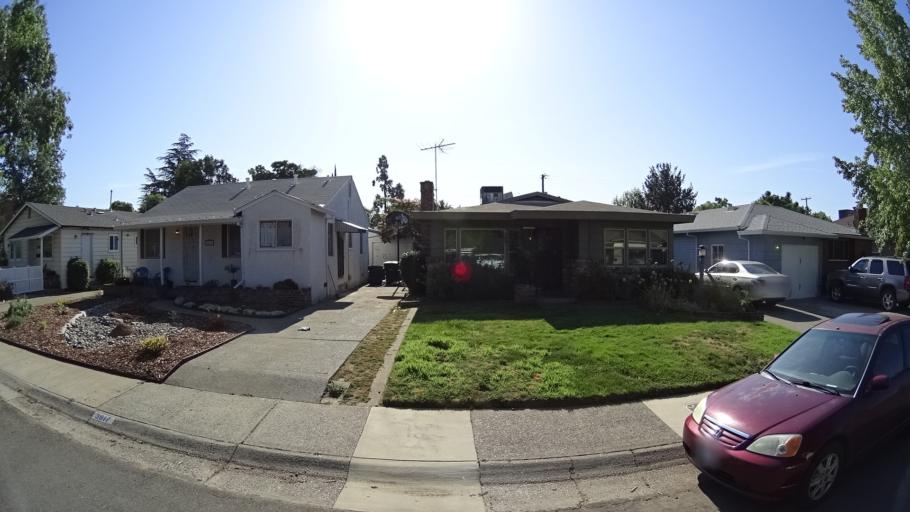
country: US
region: California
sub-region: Sacramento County
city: Florin
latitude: 38.5413
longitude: -121.4292
